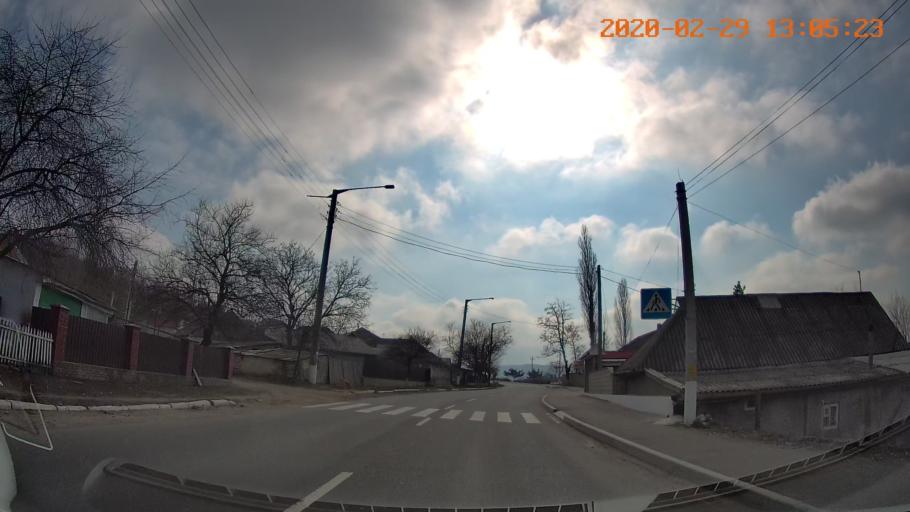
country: MD
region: Telenesti
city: Camenca
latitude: 48.0208
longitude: 28.7076
